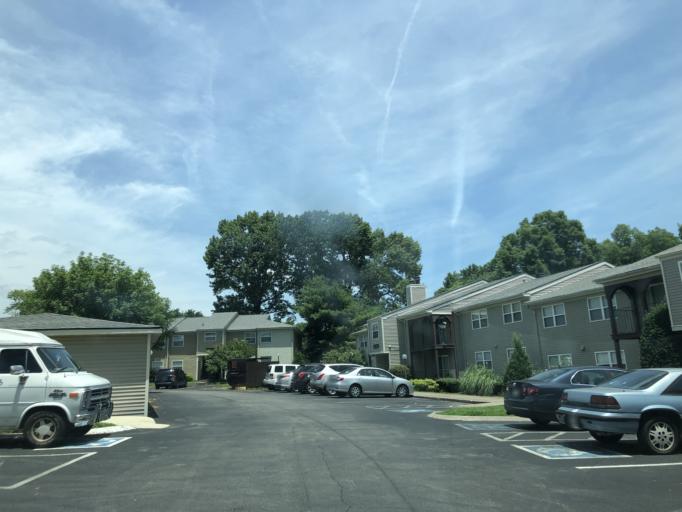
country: US
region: Tennessee
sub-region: Rutherford County
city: La Vergne
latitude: 36.0377
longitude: -86.6611
